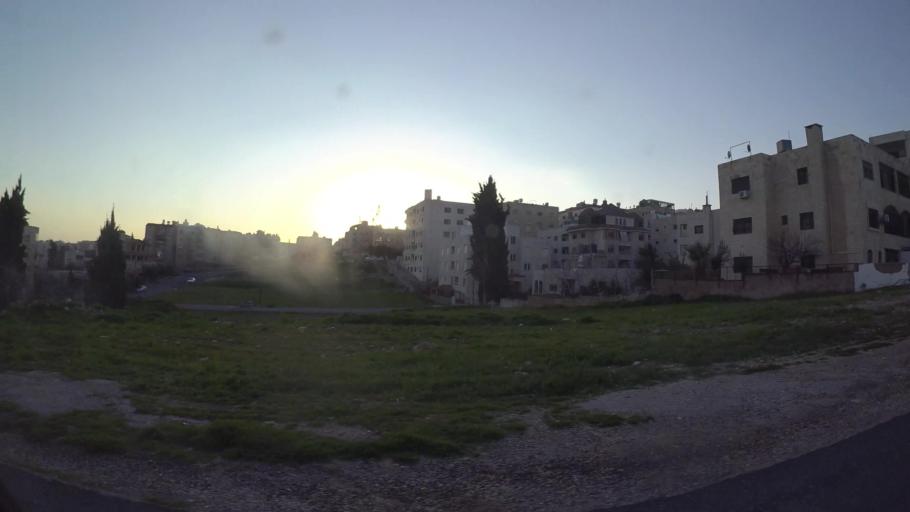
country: JO
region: Amman
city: Al Jubayhah
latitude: 32.0001
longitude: 35.8624
